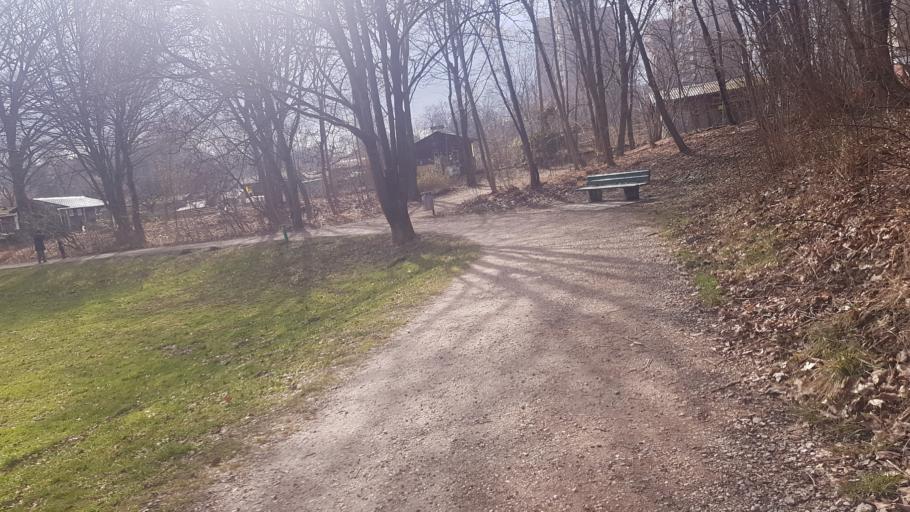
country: DE
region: Bavaria
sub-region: Upper Bavaria
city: Bogenhausen
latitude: 48.1469
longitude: 11.6188
